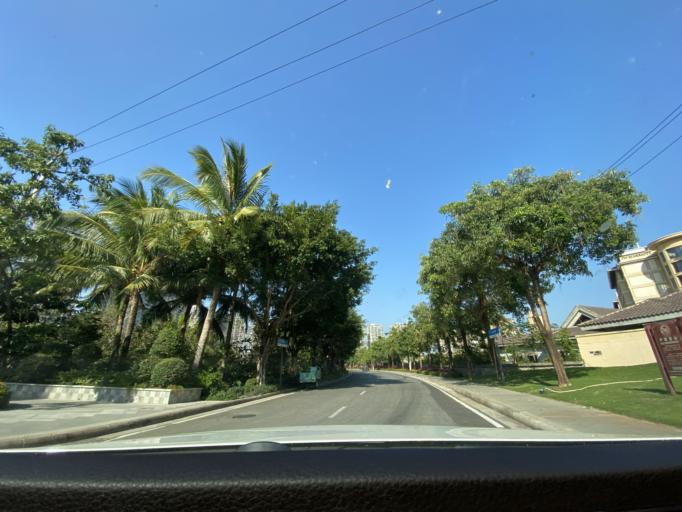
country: CN
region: Hainan
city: Yingzhou
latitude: 18.4095
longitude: 109.8807
